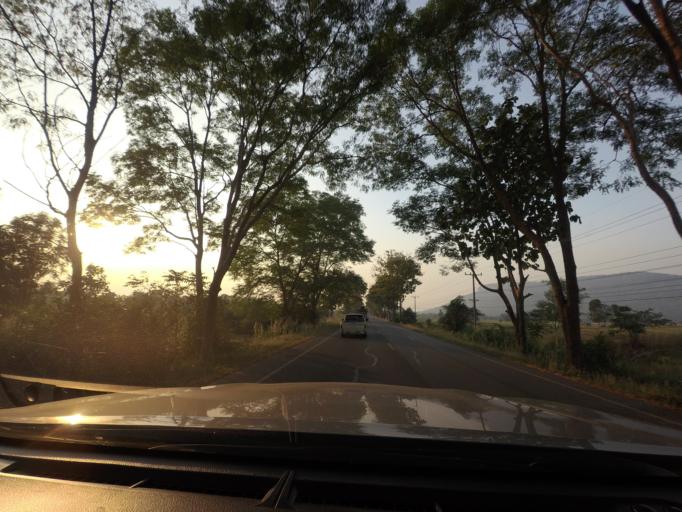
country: TH
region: Phitsanulok
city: Wang Thong
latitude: 16.7067
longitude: 100.4930
